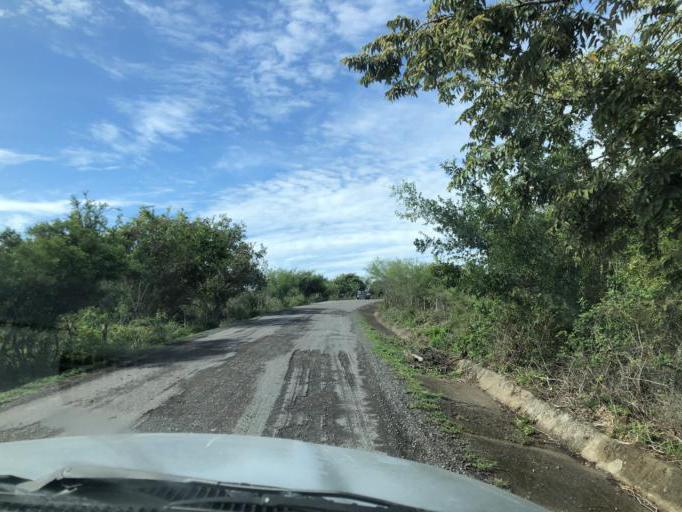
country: MX
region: Veracruz
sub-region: Alto Lucero de Gutierrez Barrios
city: Palma Sola
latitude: 19.7948
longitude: -96.5480
